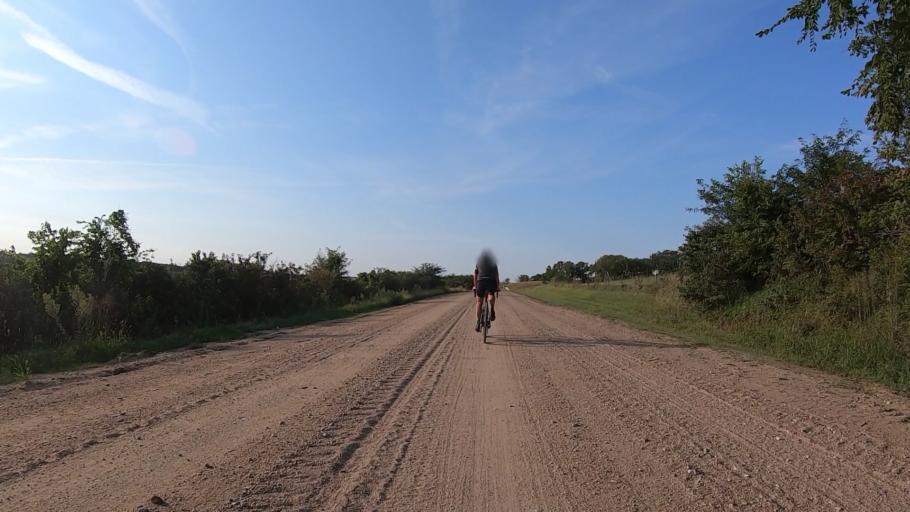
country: US
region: Kansas
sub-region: Marshall County
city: Blue Rapids
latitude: 39.6864
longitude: -96.7790
